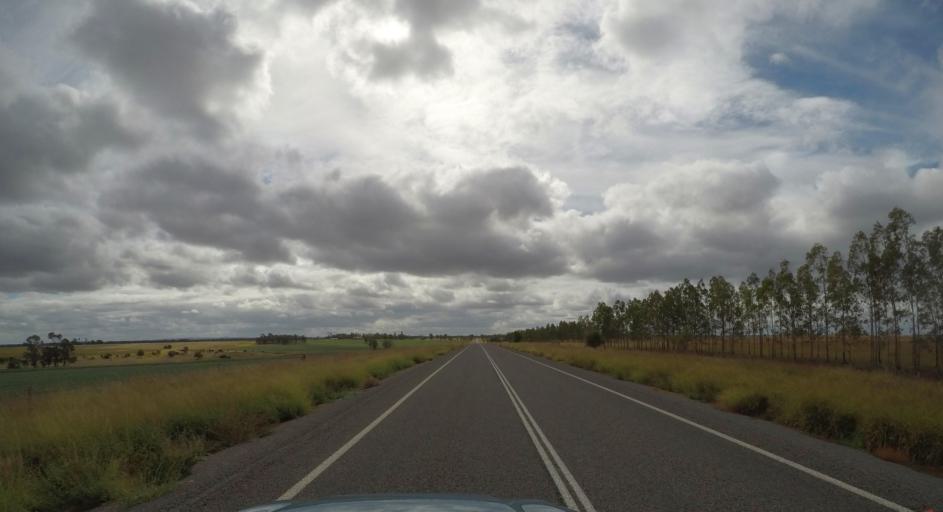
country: AU
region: Queensland
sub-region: South Burnett
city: Wondai
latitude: -26.3225
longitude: 151.2552
